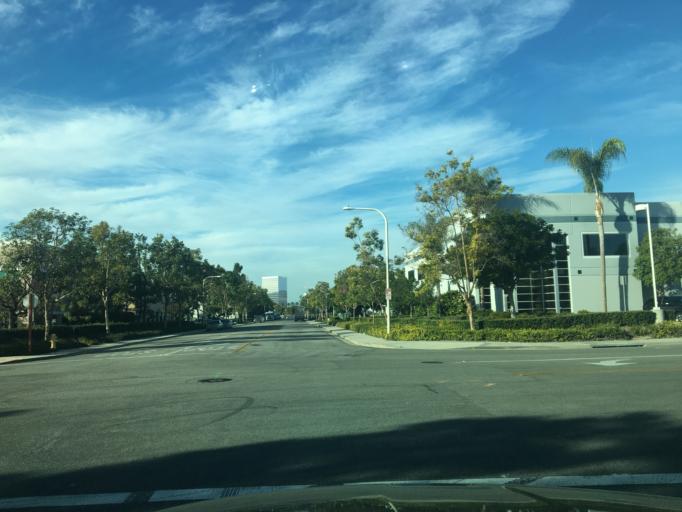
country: US
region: California
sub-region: Orange County
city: Laguna Woods
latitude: 33.6411
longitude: -117.7408
